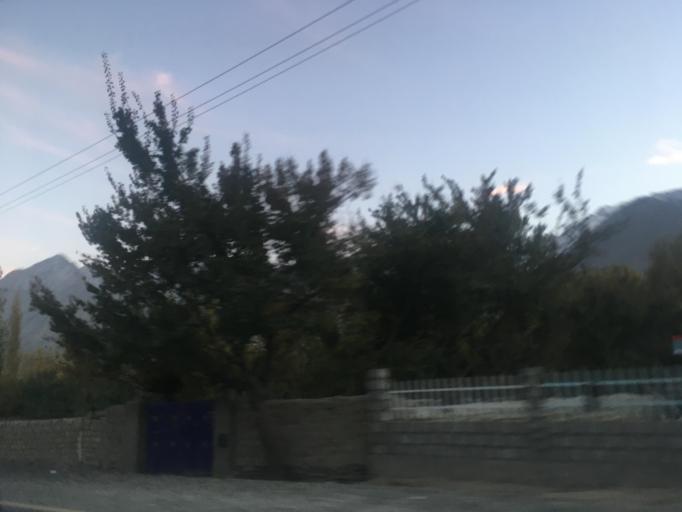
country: PK
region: Gilgit-Baltistan
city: Skardu
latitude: 35.3013
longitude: 75.5532
